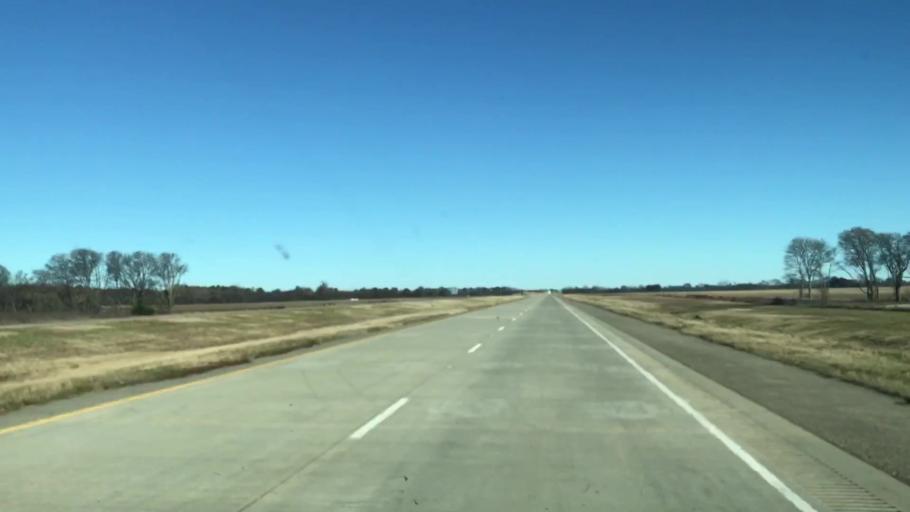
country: US
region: Louisiana
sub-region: Caddo Parish
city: Vivian
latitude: 32.8665
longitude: -93.8601
